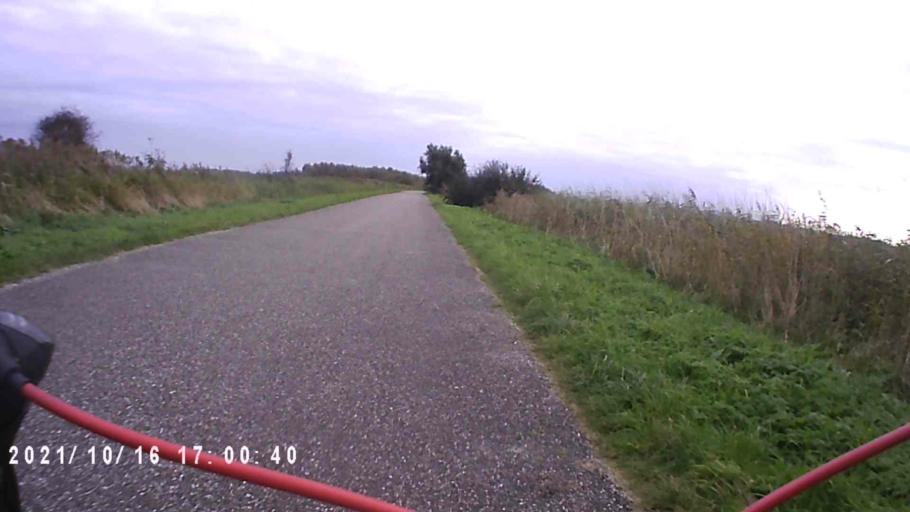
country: NL
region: Friesland
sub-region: Gemeente Dongeradeel
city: Anjum
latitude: 53.3524
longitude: 6.1521
